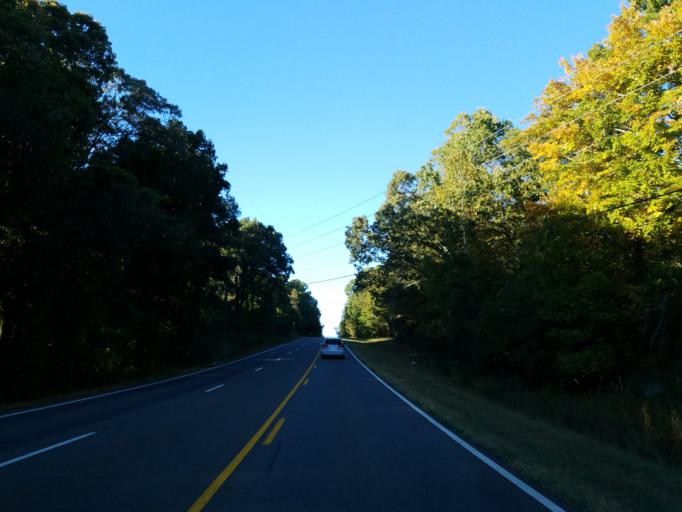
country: US
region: Georgia
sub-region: Pickens County
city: Nelson
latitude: 34.4030
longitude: -84.3843
